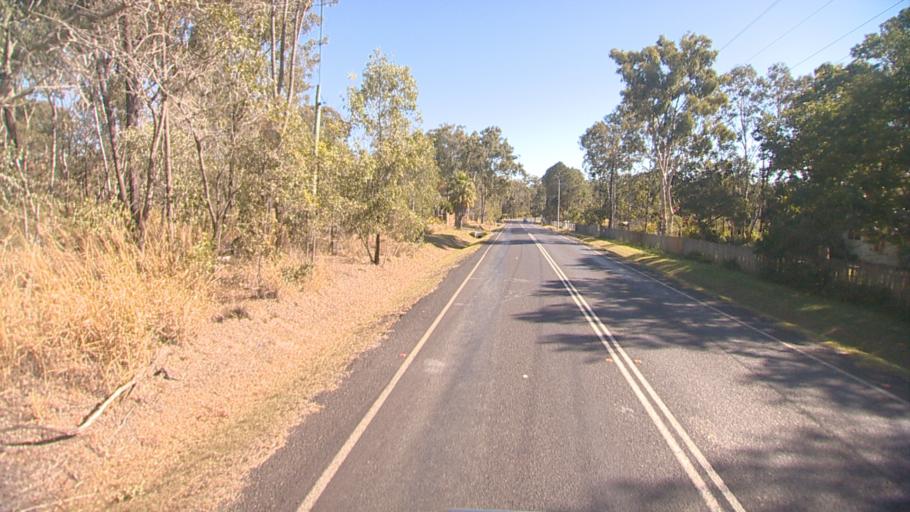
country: AU
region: Queensland
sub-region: Logan
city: Park Ridge South
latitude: -27.7239
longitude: 153.0147
